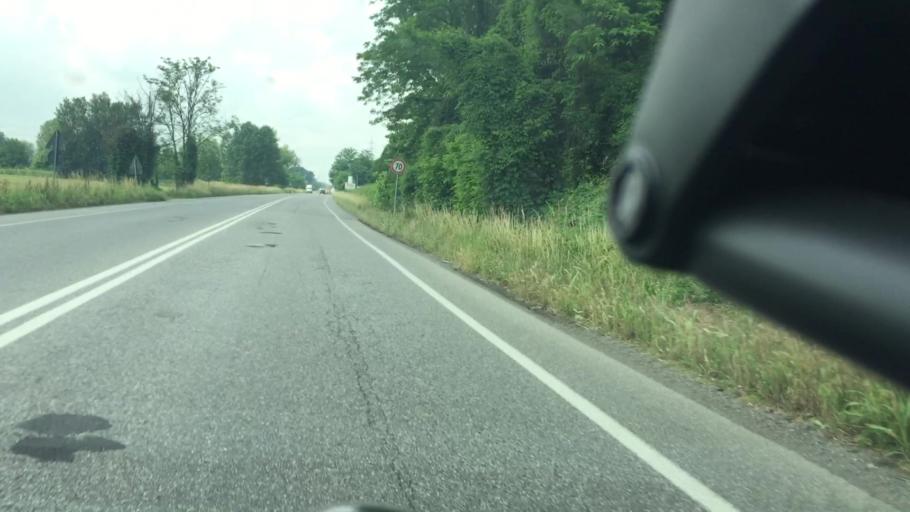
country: IT
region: Lombardy
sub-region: Citta metropolitana di Milano
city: Gorgonzola
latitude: 45.5286
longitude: 9.4161
